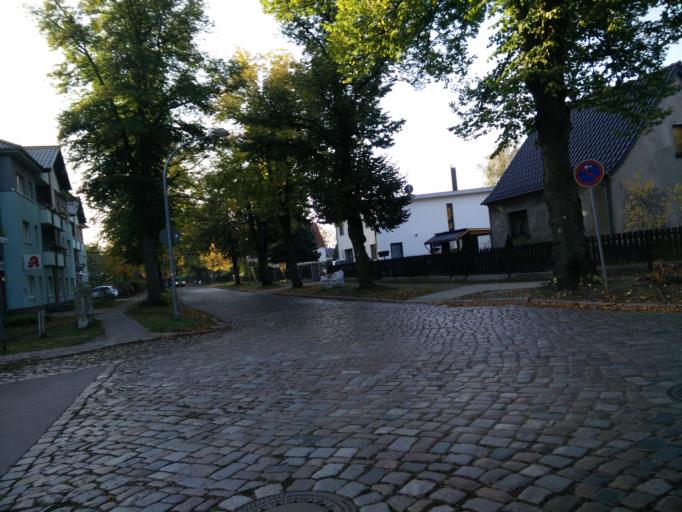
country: DE
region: Brandenburg
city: Falkensee
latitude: 52.5737
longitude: 13.0915
